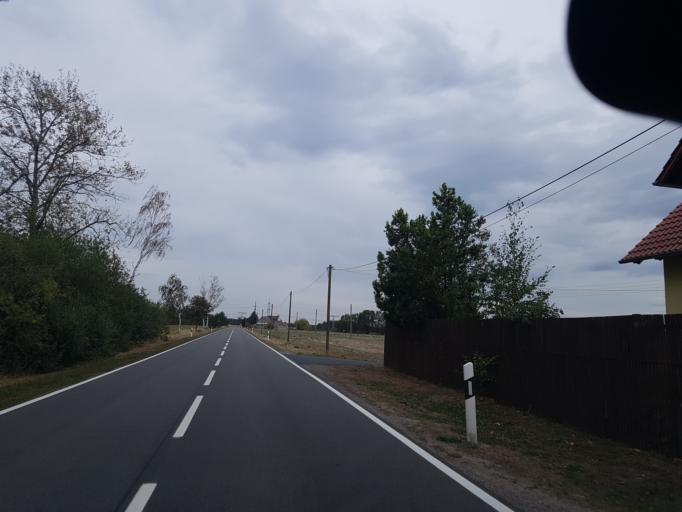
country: DE
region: Saxony-Anhalt
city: Annaburg
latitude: 51.7870
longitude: 13.0252
